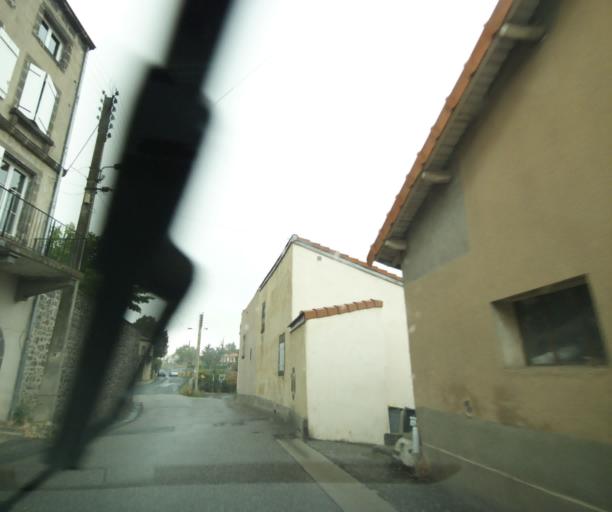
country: FR
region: Auvergne
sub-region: Departement du Puy-de-Dome
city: Chateaugay
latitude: 45.8513
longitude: 3.0855
